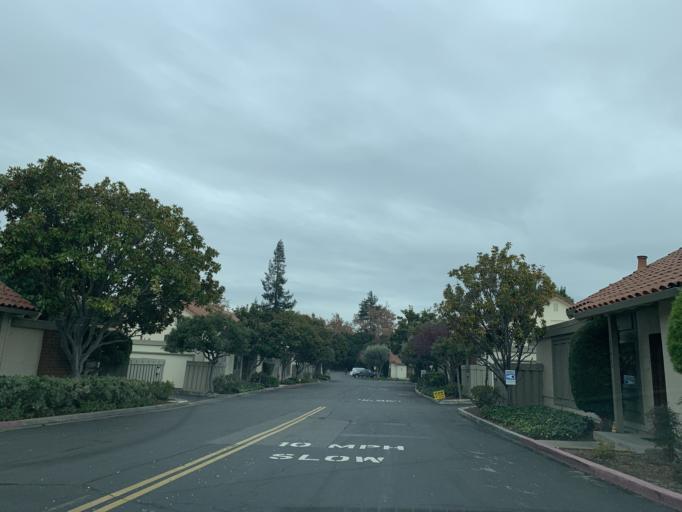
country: US
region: California
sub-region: Santa Clara County
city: Cupertino
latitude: 37.3374
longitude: -122.0637
